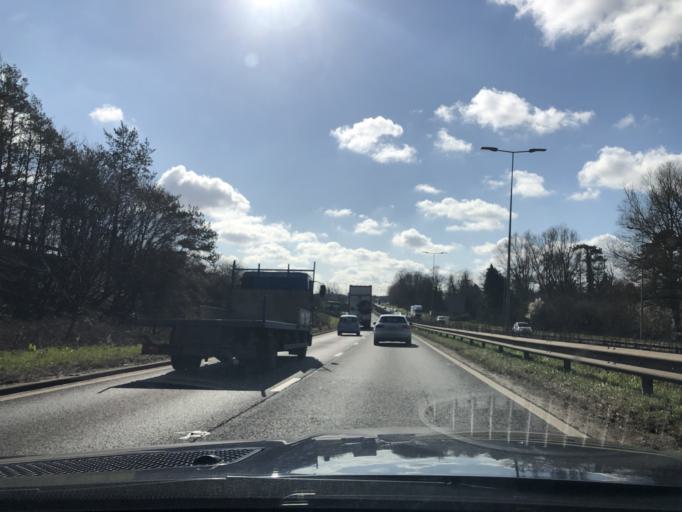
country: GB
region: England
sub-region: Northamptonshire
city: Hardingstone
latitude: 52.1988
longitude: -0.8928
